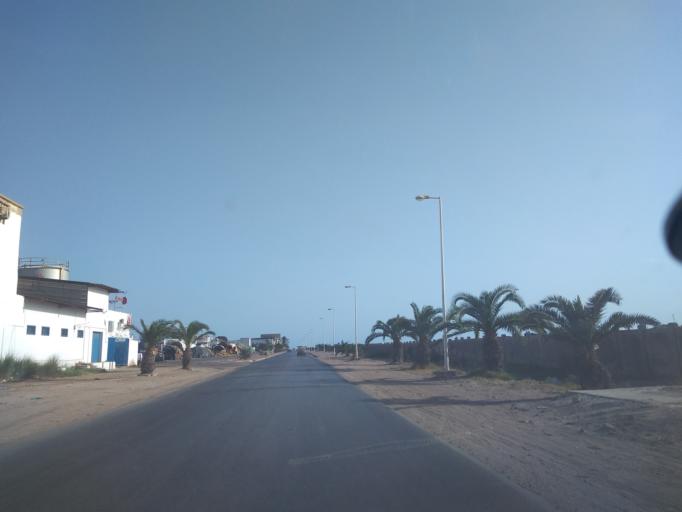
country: TN
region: Safaqis
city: Sfax
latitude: 34.7185
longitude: 10.7609
